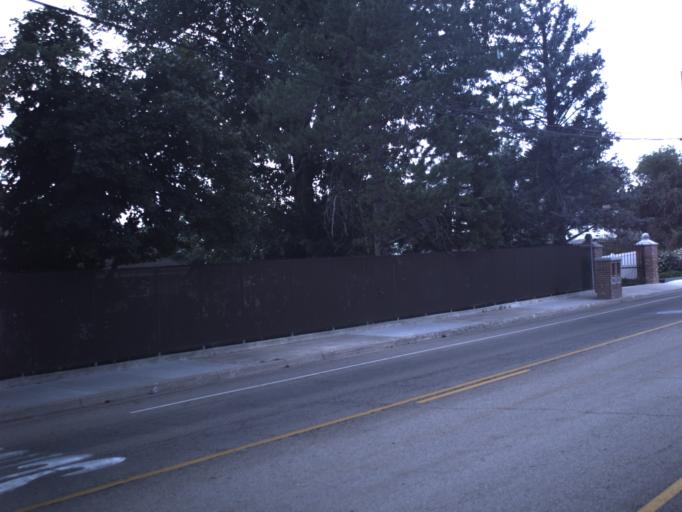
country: US
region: Utah
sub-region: Davis County
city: Centerville
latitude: 40.9328
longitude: -111.8789
